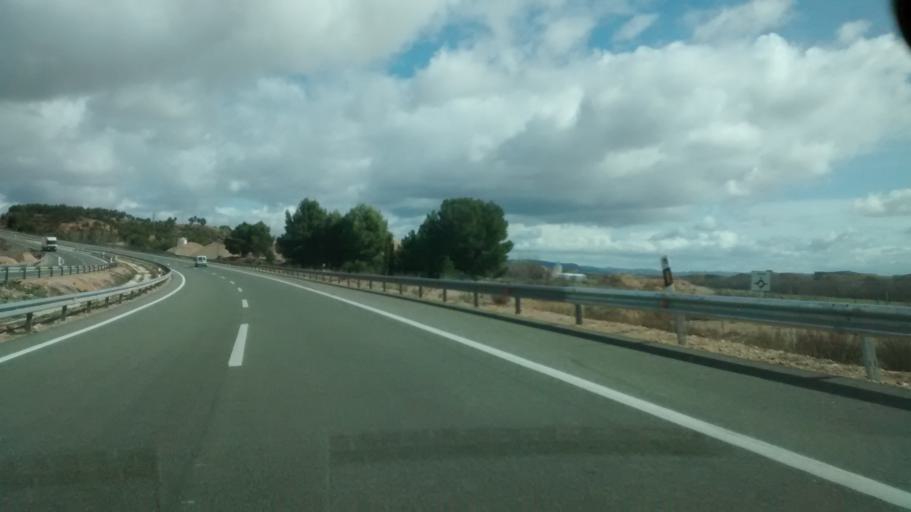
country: ES
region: Aragon
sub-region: Provincia de Zaragoza
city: Ariza
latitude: 41.3104
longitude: -2.0774
